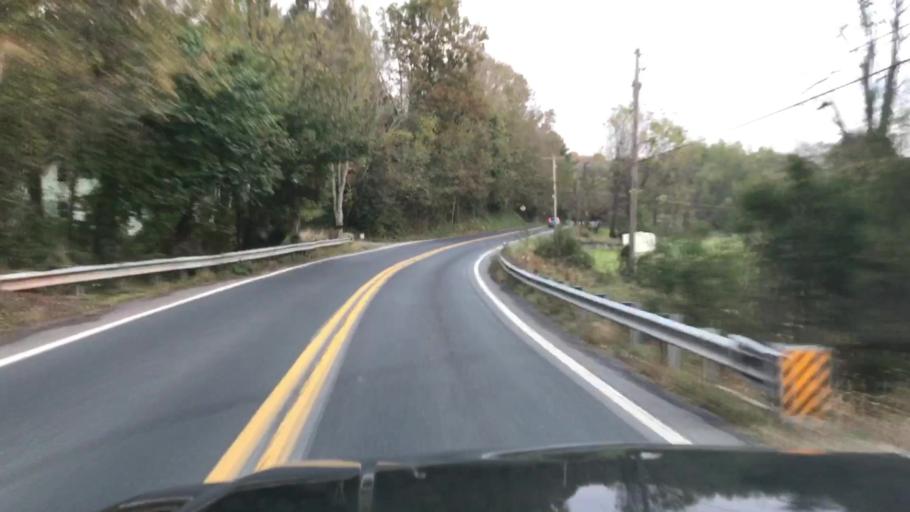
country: US
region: Pennsylvania
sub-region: Cumberland County
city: Shiremanstown
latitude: 40.1804
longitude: -76.9282
